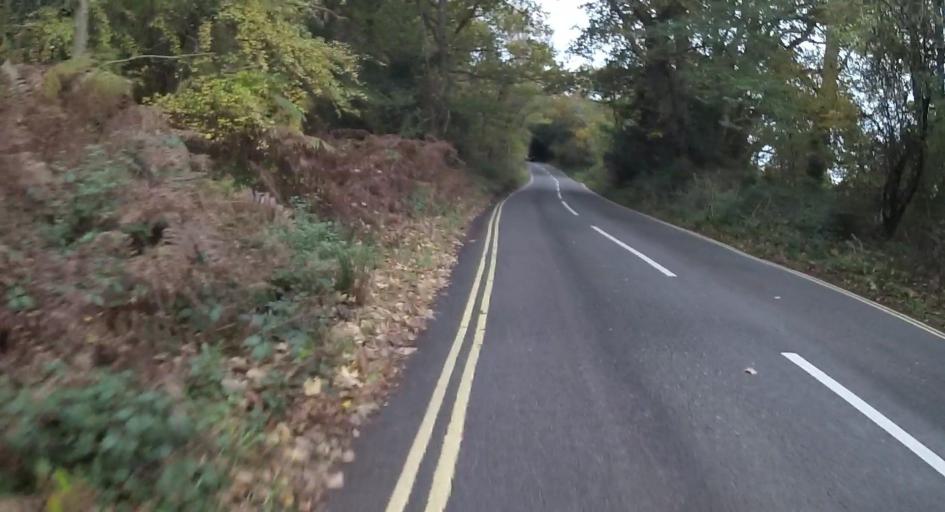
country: GB
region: England
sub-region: Surrey
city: Churt
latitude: 51.1631
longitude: -0.7941
